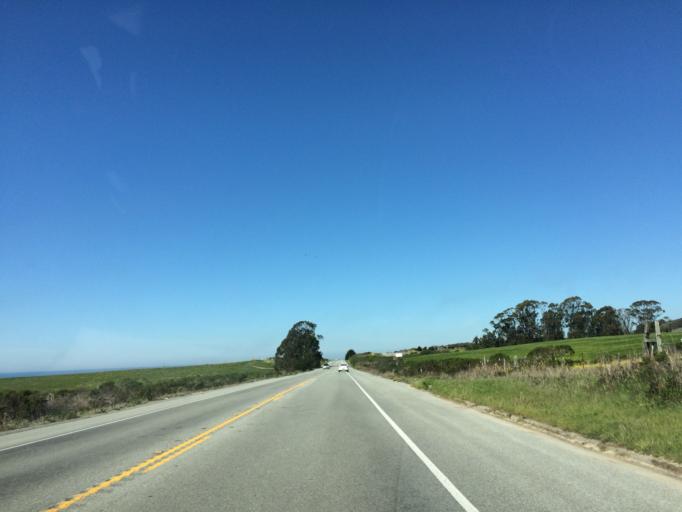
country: US
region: California
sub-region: San Mateo County
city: Half Moon Bay
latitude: 37.3906
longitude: -122.4086
